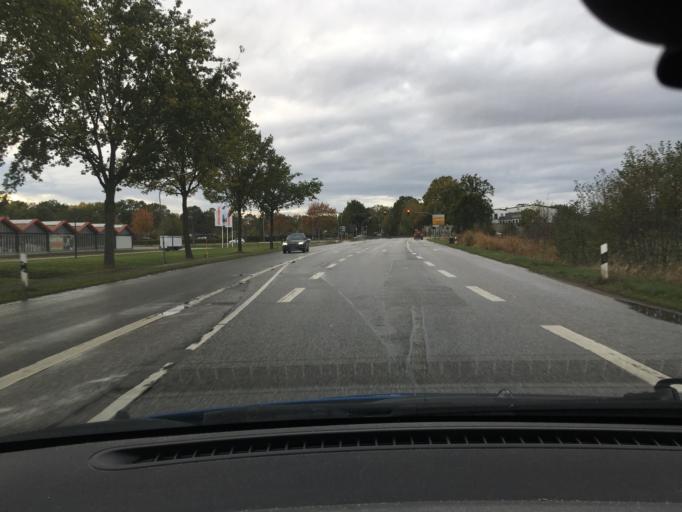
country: DE
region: Schleswig-Holstein
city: Bornsen
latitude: 53.4902
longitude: 10.2734
